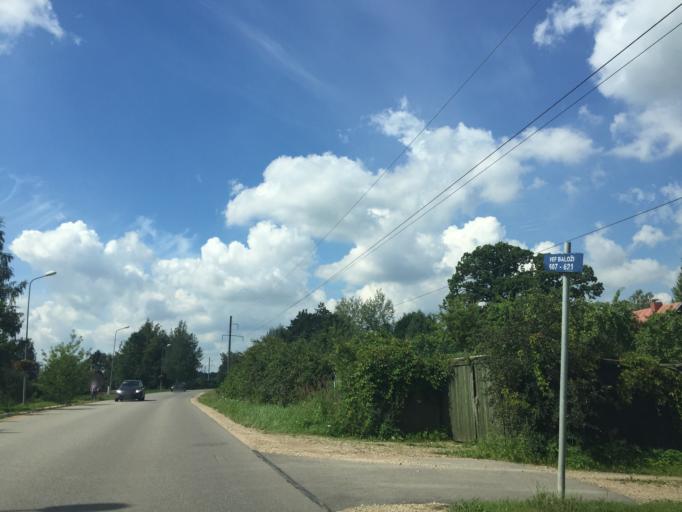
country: LV
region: Kekava
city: Balozi
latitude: 56.8602
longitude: 24.0767
